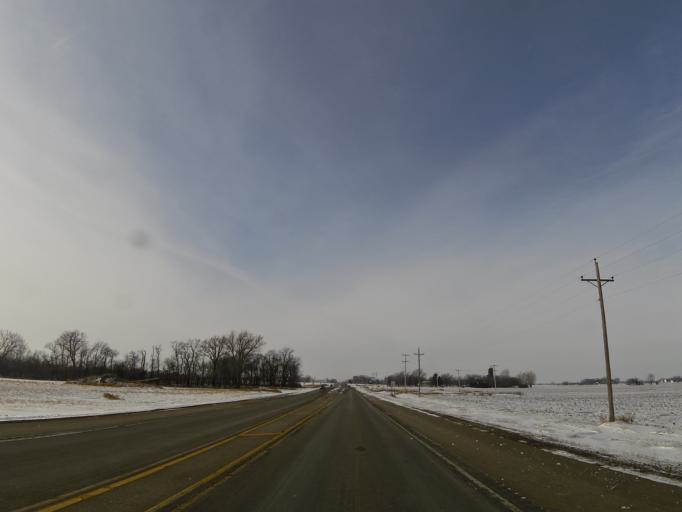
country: US
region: Minnesota
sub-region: McLeod County
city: Lester Prairie
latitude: 44.9067
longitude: -94.1162
